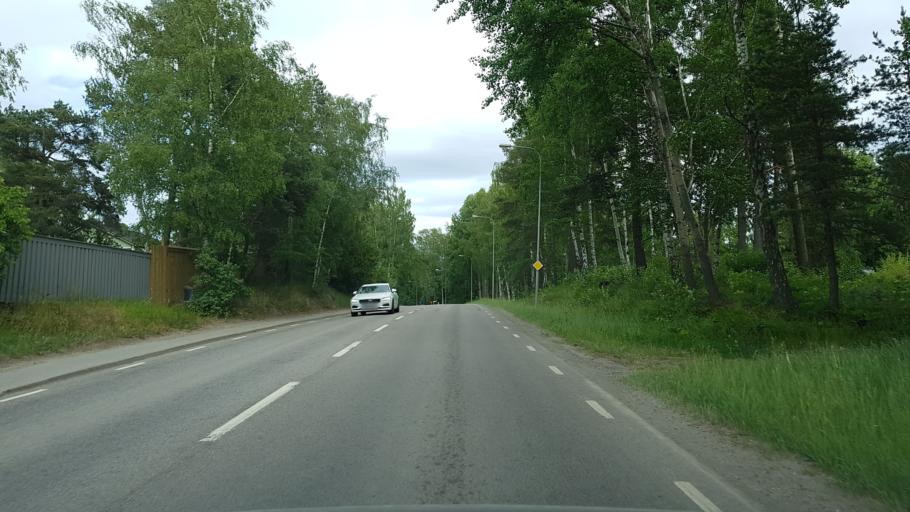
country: SE
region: Stockholm
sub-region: Haninge Kommun
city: Jordbro
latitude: 59.1220
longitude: 18.0923
